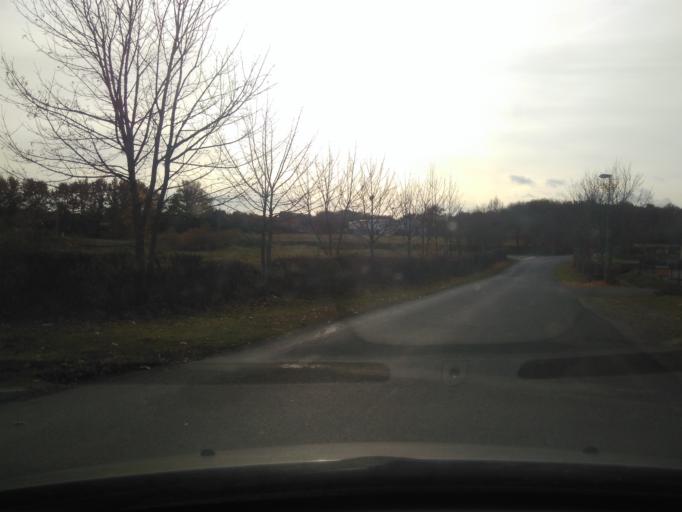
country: FR
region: Pays de la Loire
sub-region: Departement de la Vendee
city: Saint-Florent-des-Bois
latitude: 46.5876
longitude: -1.3070
